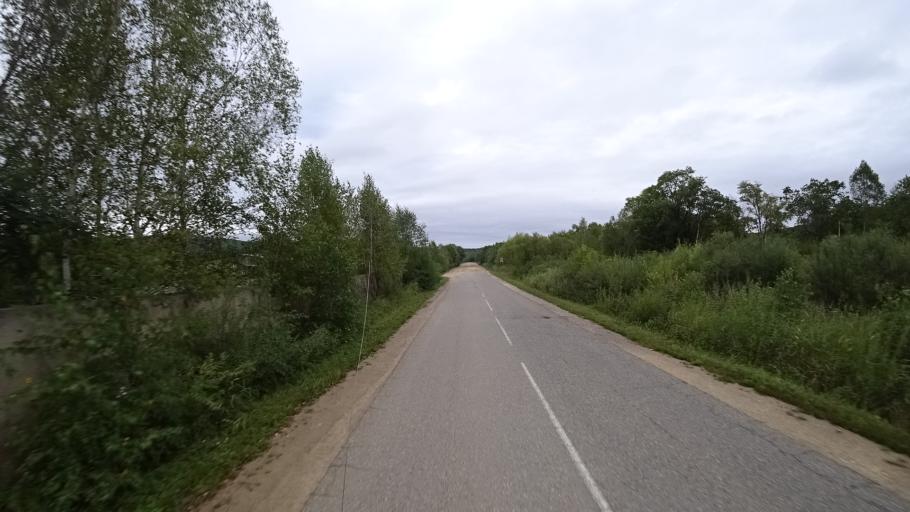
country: RU
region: Primorskiy
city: Rettikhovka
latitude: 44.1679
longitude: 132.7908
